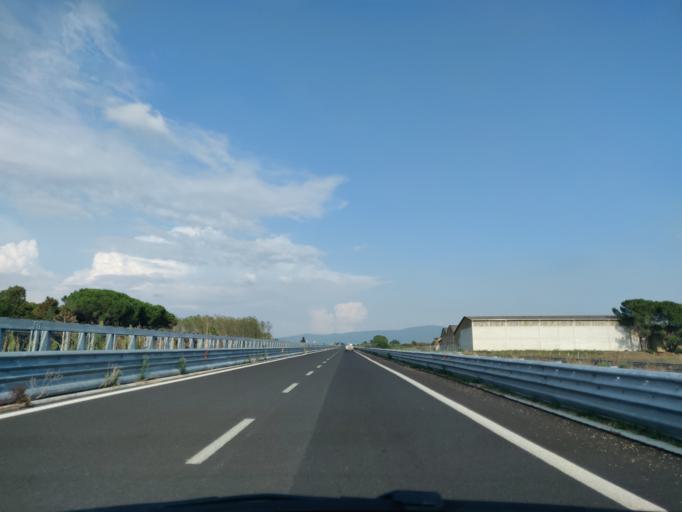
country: IT
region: Latium
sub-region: Provincia di Viterbo
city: Blera
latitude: 42.3004
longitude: 11.9754
